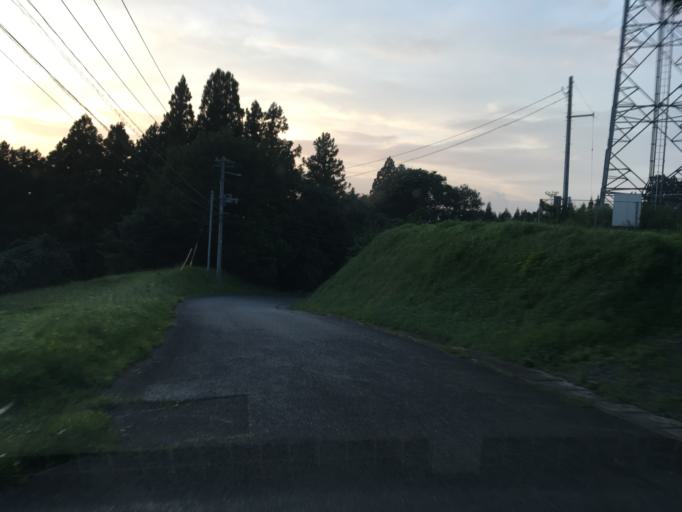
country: JP
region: Iwate
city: Ichinoseki
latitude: 38.8424
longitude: 141.2867
